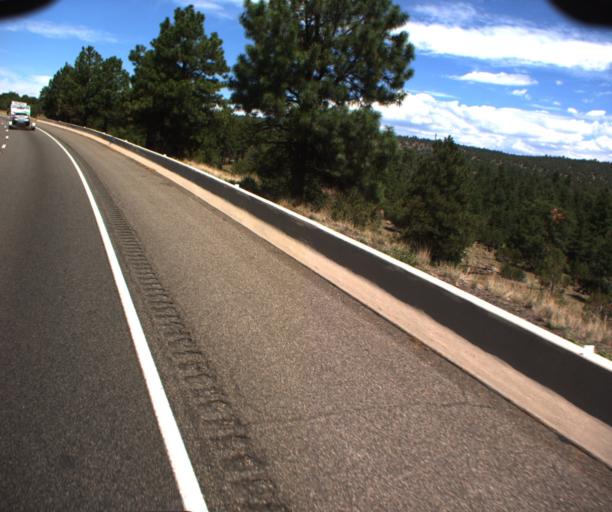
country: US
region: Arizona
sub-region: Yavapai County
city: Village of Oak Creek (Big Park)
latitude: 34.7990
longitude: -111.5912
